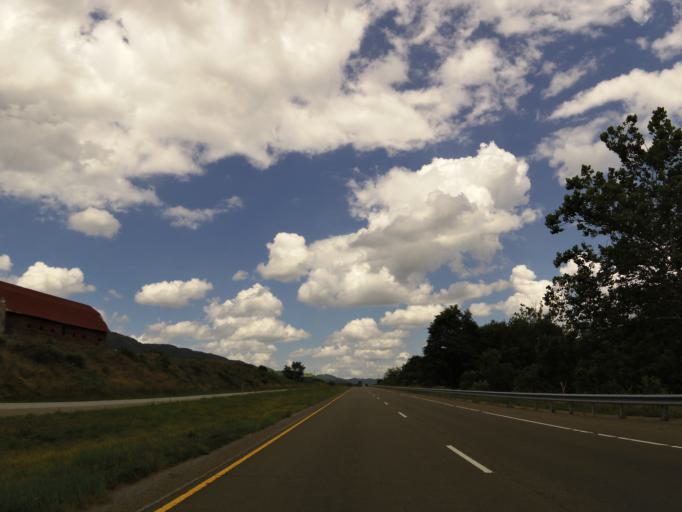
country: US
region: Kentucky
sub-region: Harlan County
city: Loyall
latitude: 36.6403
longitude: -83.4254
